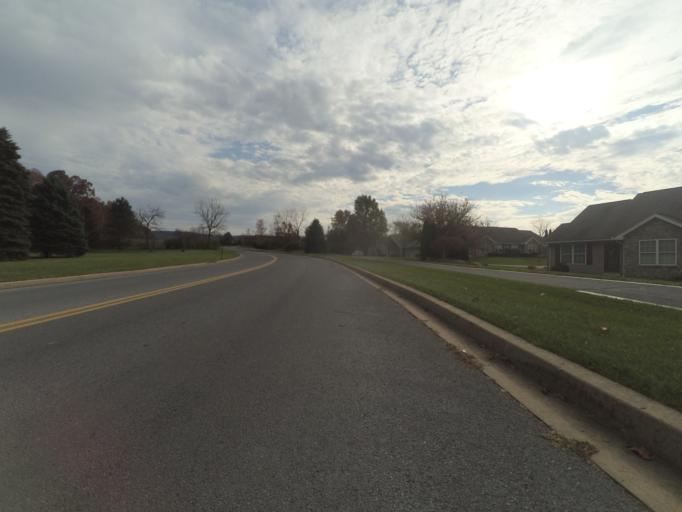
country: US
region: Pennsylvania
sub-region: Centre County
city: Lemont
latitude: 40.7870
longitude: -77.8211
